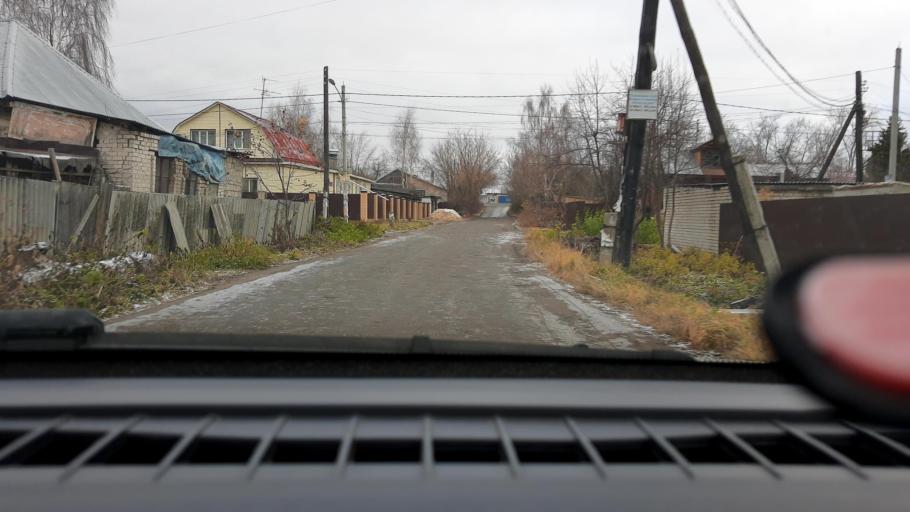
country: RU
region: Nizjnij Novgorod
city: Burevestnik
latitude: 56.2042
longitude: 43.7923
